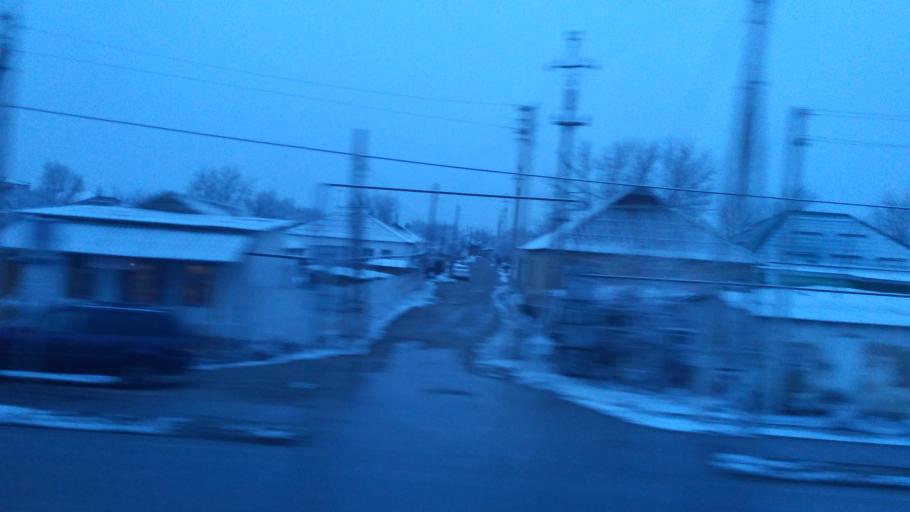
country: KZ
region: Ongtustik Qazaqstan
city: Shymkent
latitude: 42.3770
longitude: 69.4982
